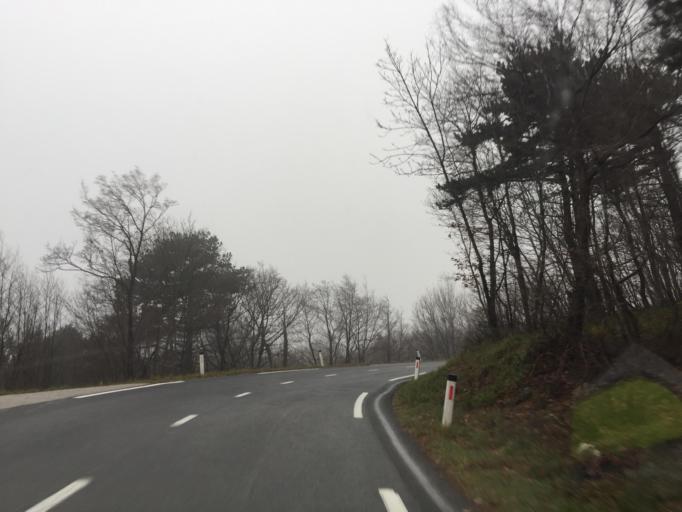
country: SI
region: Ajdovscina
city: Lokavec
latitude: 45.9211
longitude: 13.8911
